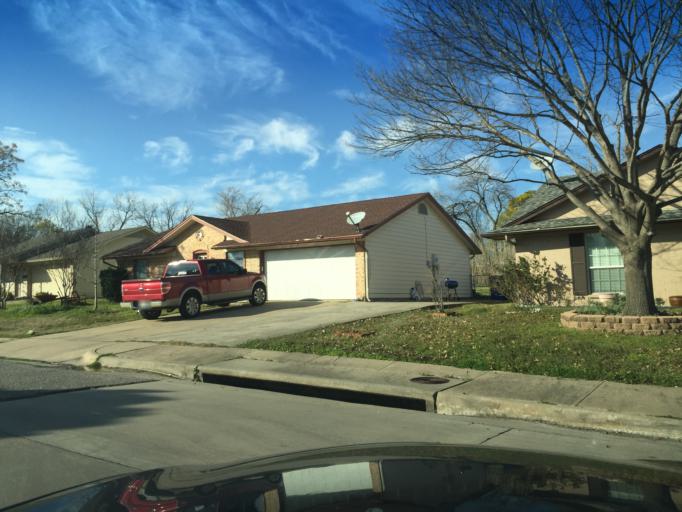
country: US
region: Texas
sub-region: Dallas County
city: Carrollton
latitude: 32.9799
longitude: -96.8850
